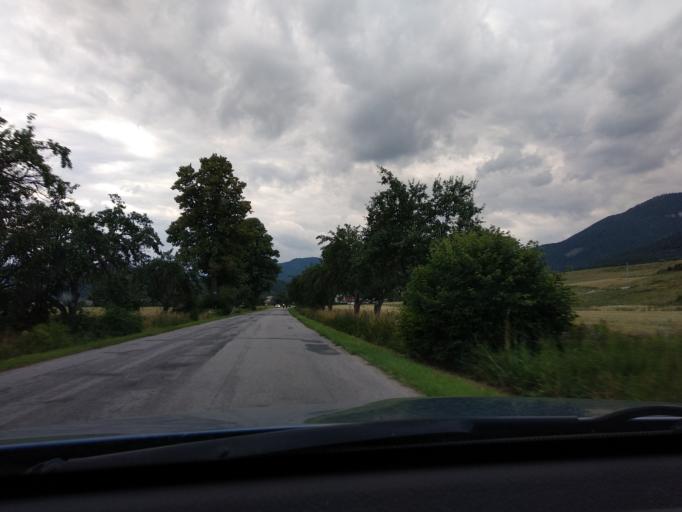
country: SK
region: Zilinsky
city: Ruzomberok
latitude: 49.0929
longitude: 19.3698
